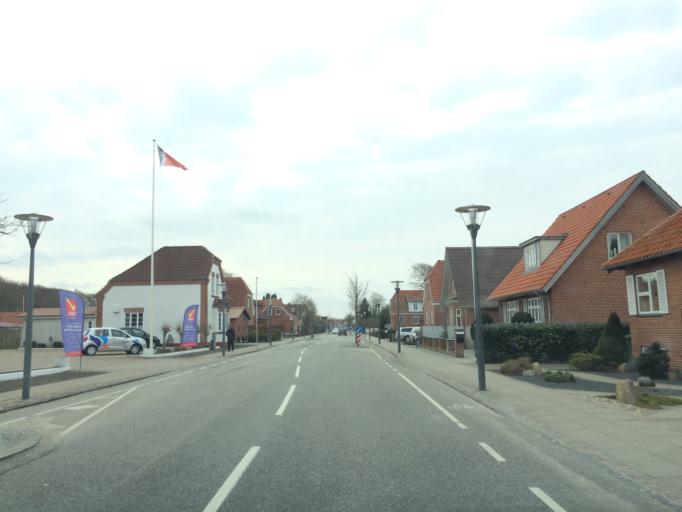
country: DK
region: Central Jutland
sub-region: Ringkobing-Skjern Kommune
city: Tarm
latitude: 55.9134
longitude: 8.5196
